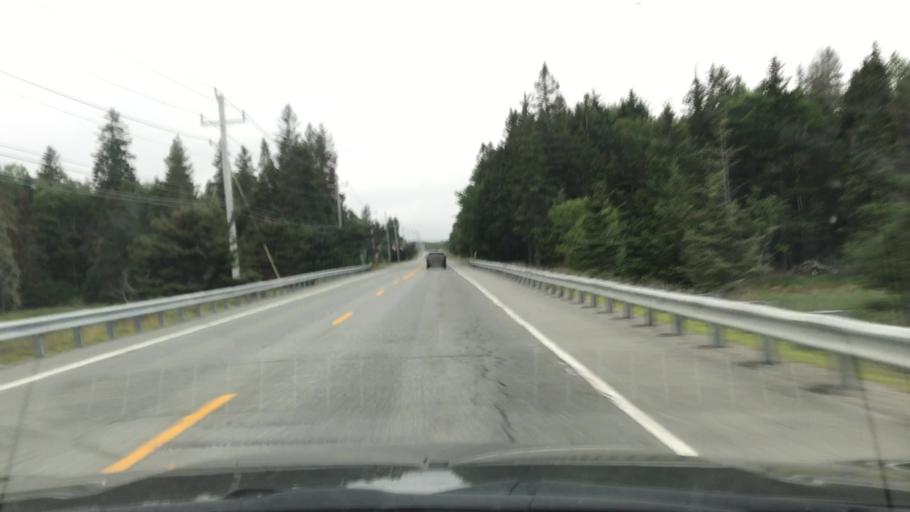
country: US
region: Maine
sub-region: Hancock County
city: Trenton
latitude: 44.4254
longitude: -68.3655
